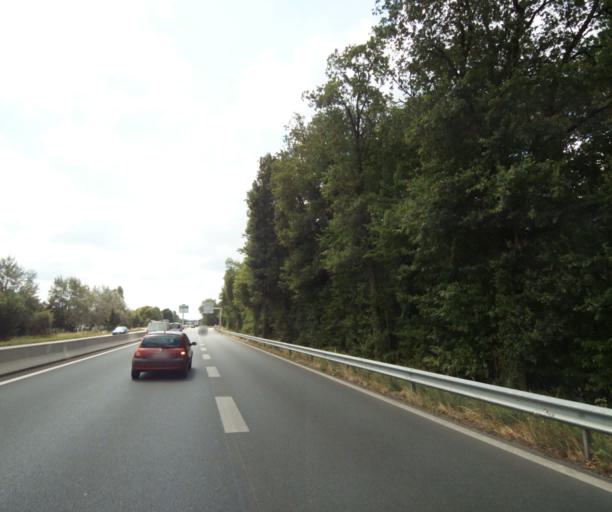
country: FR
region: Centre
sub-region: Departement du Loiret
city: Olivet
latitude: 47.8338
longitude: 1.9174
